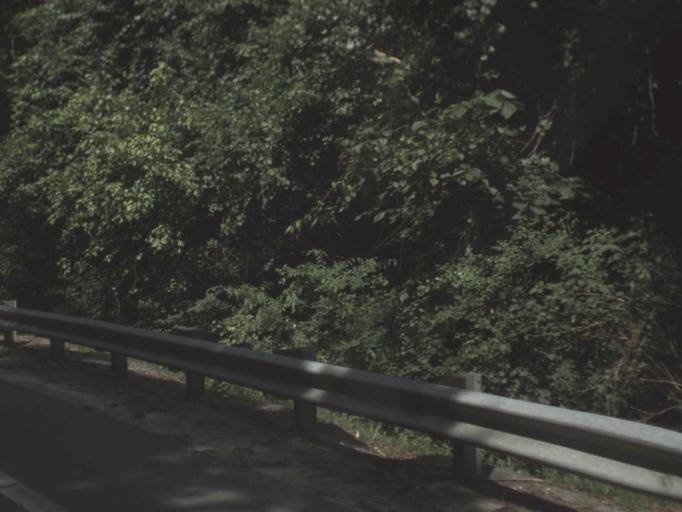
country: US
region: Florida
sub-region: Alachua County
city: High Springs
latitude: 29.8656
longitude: -82.7398
